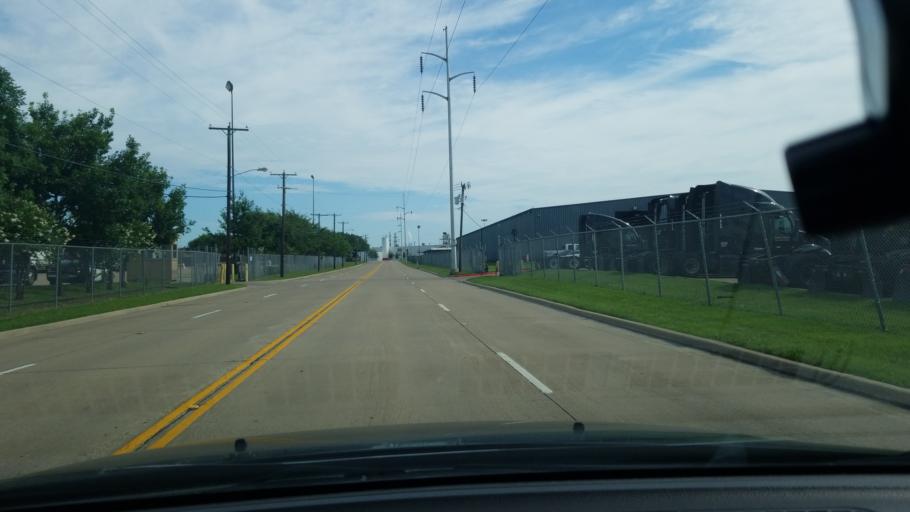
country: US
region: Texas
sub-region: Dallas County
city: Balch Springs
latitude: 32.7708
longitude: -96.6568
